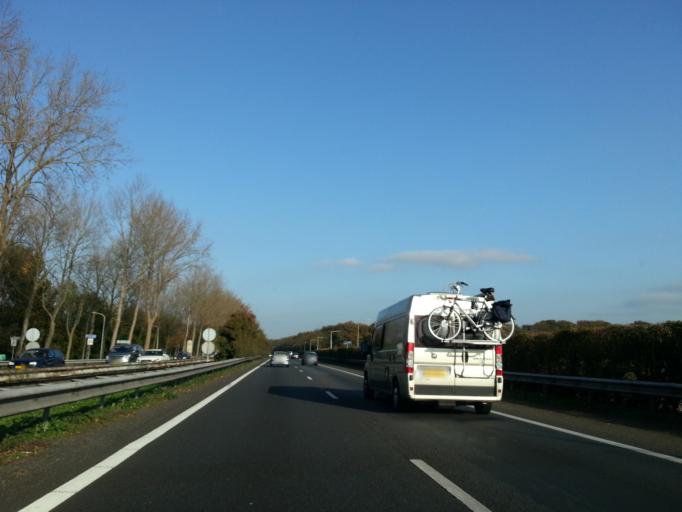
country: NL
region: South Holland
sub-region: Gemeente Wassenaar
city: Wassenaar
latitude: 52.1426
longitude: 4.4173
